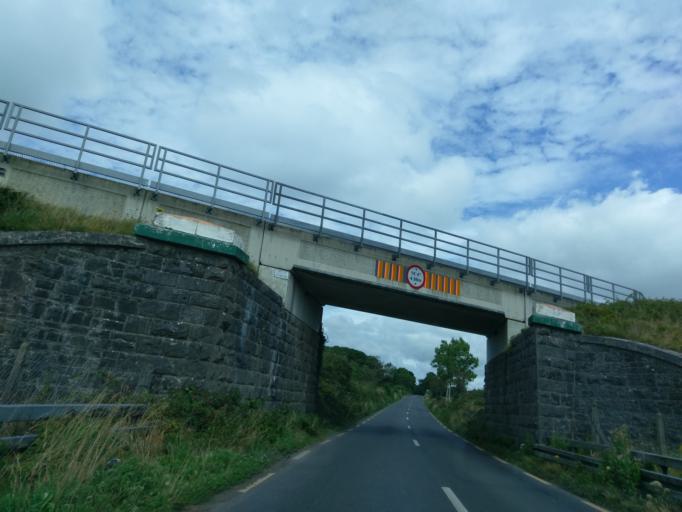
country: IE
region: Connaught
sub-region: County Galway
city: Oranmore
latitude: 53.2784
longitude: -8.8503
